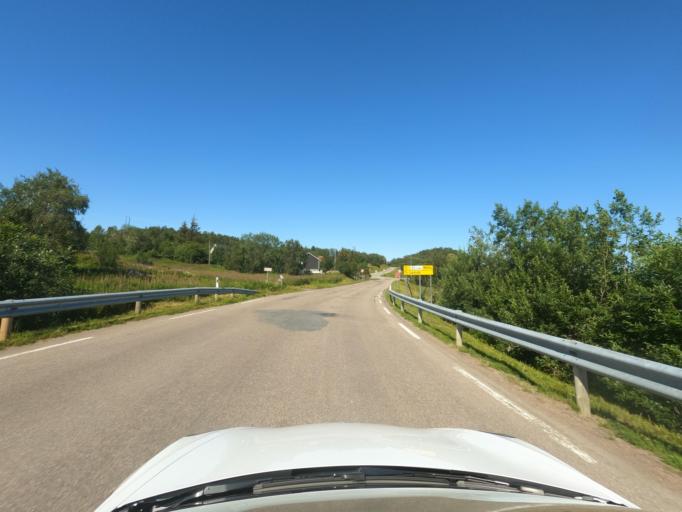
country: NO
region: Nordland
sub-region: Hadsel
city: Melbu
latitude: 68.4280
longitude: 14.8196
